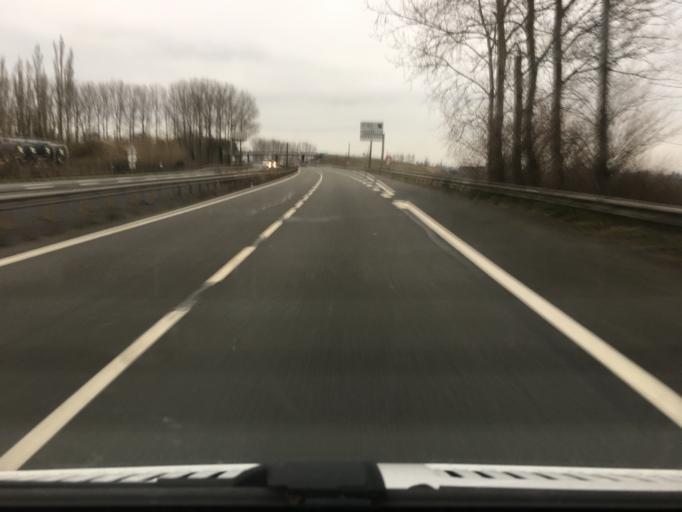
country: FR
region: Nord-Pas-de-Calais
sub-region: Departement du Nord
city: Cappelle-la-Grande
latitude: 50.9955
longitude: 2.3332
